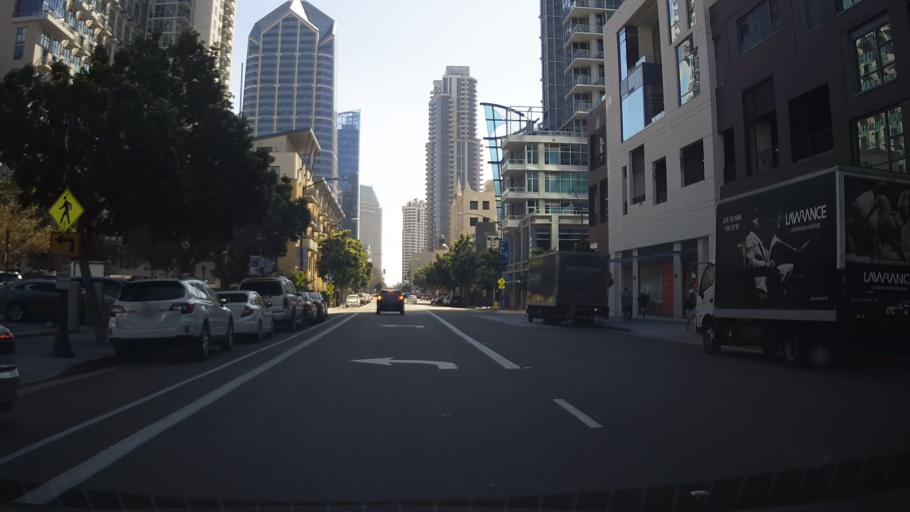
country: US
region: California
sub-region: San Diego County
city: San Diego
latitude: 32.7195
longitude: -117.1692
